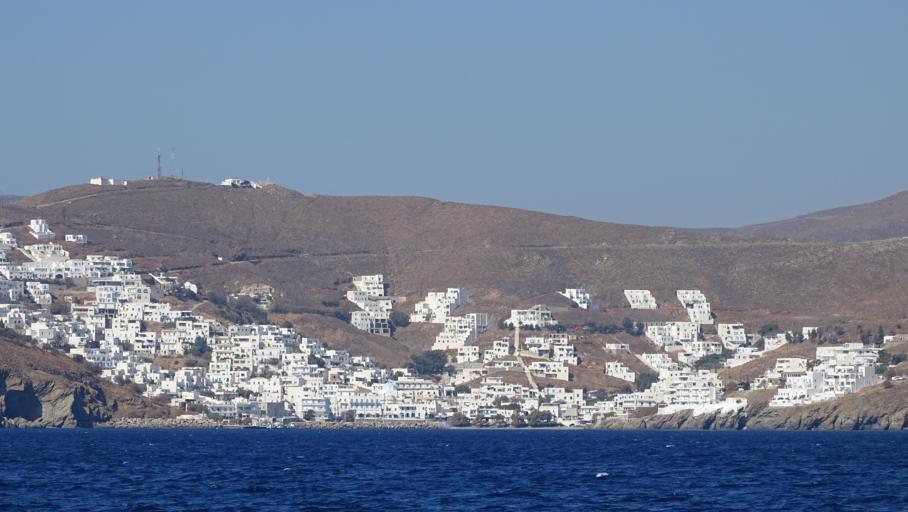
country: GR
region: South Aegean
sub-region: Nomos Dodekanisou
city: Astypalaia
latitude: 36.5464
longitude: 26.3806
